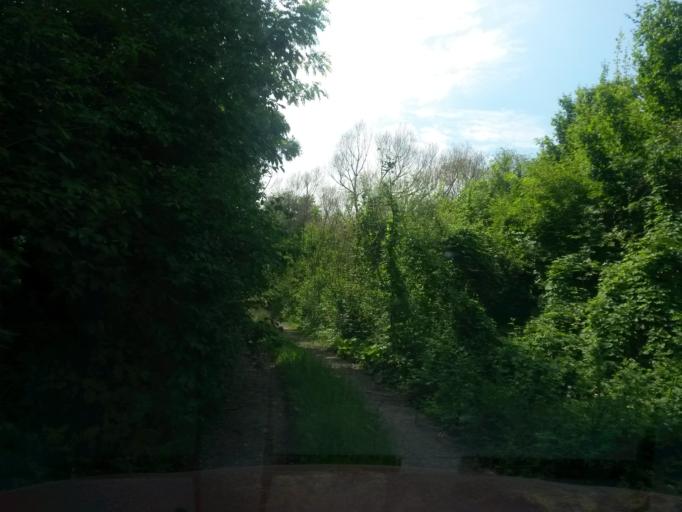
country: SK
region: Kosicky
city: Secovce
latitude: 48.6278
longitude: 21.4977
